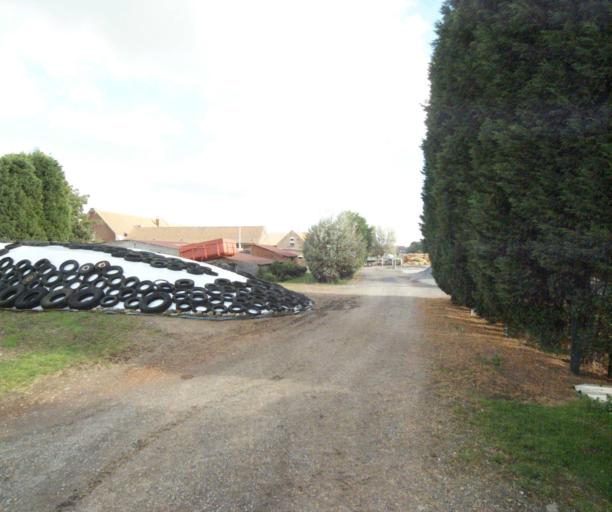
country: FR
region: Nord-Pas-de-Calais
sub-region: Departement du Nord
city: Houplines
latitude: 50.6708
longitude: 2.9190
